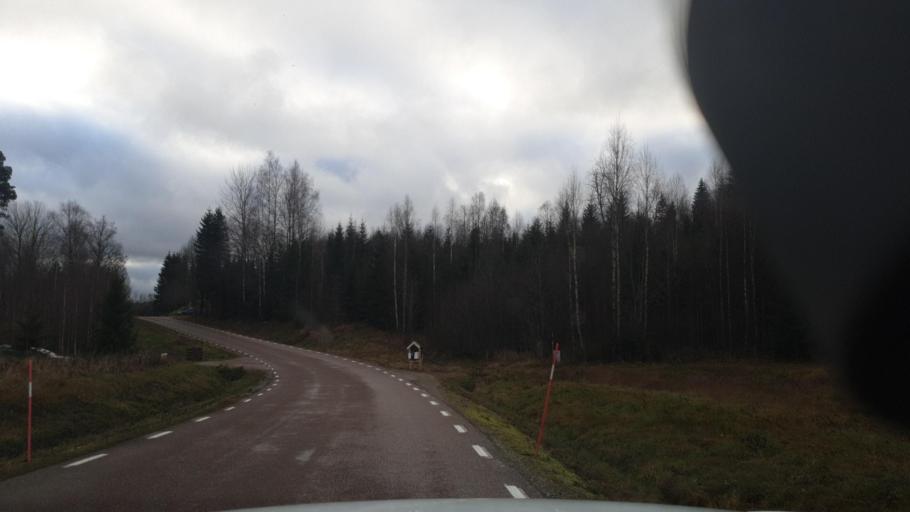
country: SE
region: Vaermland
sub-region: Arvika Kommun
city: Arvika
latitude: 59.7660
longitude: 12.8209
